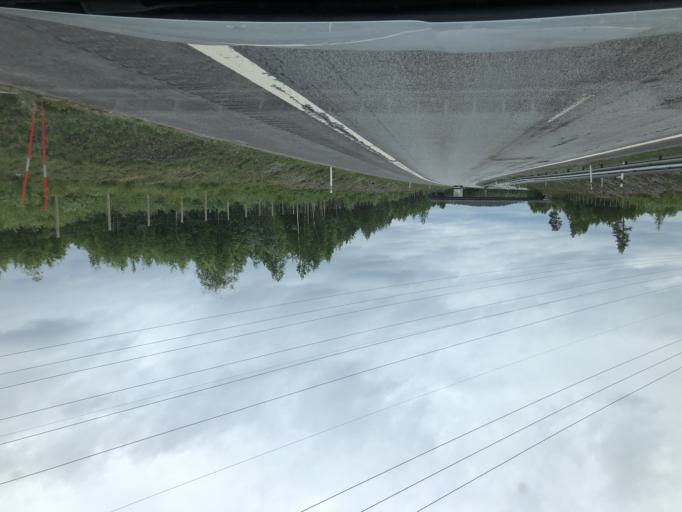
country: SE
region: Norrbotten
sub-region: Pitea Kommun
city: Pitea
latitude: 65.3483
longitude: 21.4381
